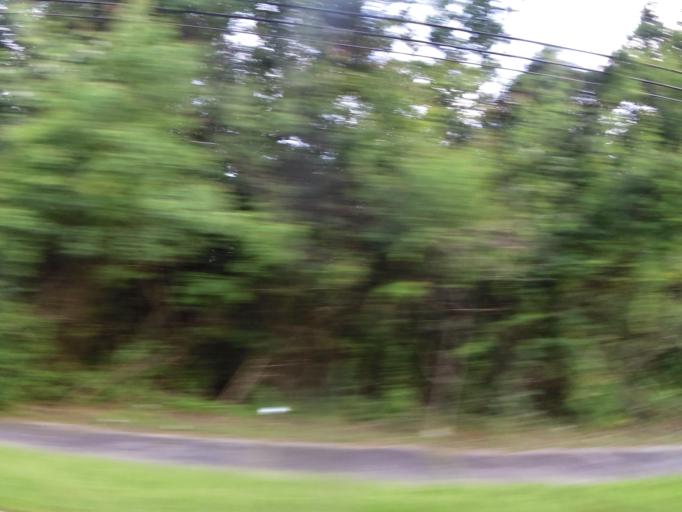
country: US
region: Florida
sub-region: Duval County
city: Jacksonville
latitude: 30.3714
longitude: -81.7828
